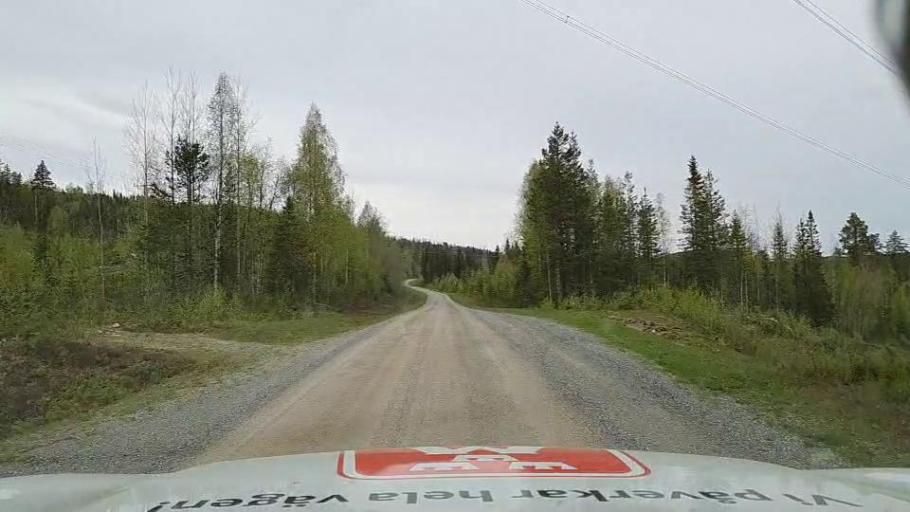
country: SE
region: Jaemtland
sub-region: Bergs Kommun
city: Hoverberg
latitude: 62.5312
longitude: 14.7079
